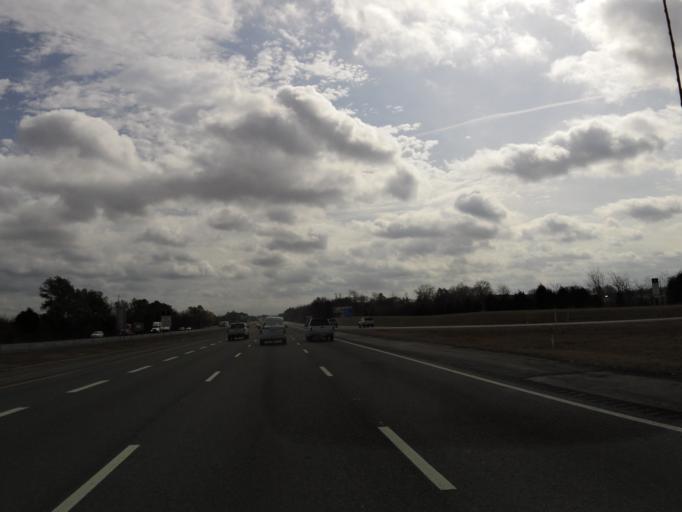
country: US
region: Tennessee
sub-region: Rutherford County
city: Murfreesboro
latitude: 35.8803
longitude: -86.4717
